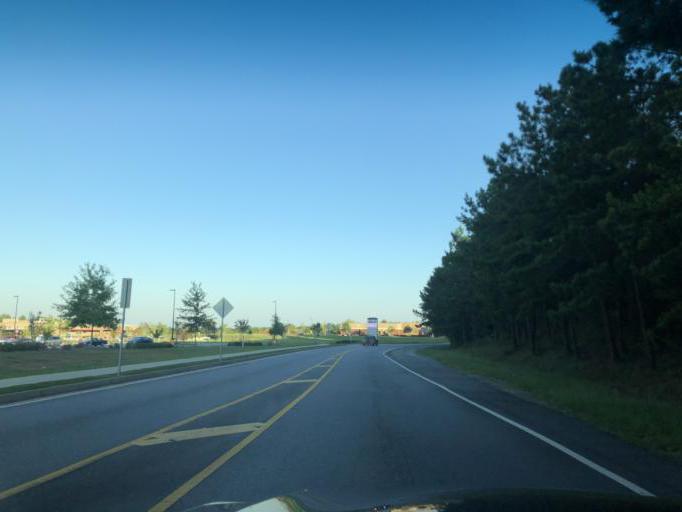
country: US
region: Georgia
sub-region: Muscogee County
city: Columbus
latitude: 32.5518
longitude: -84.8975
